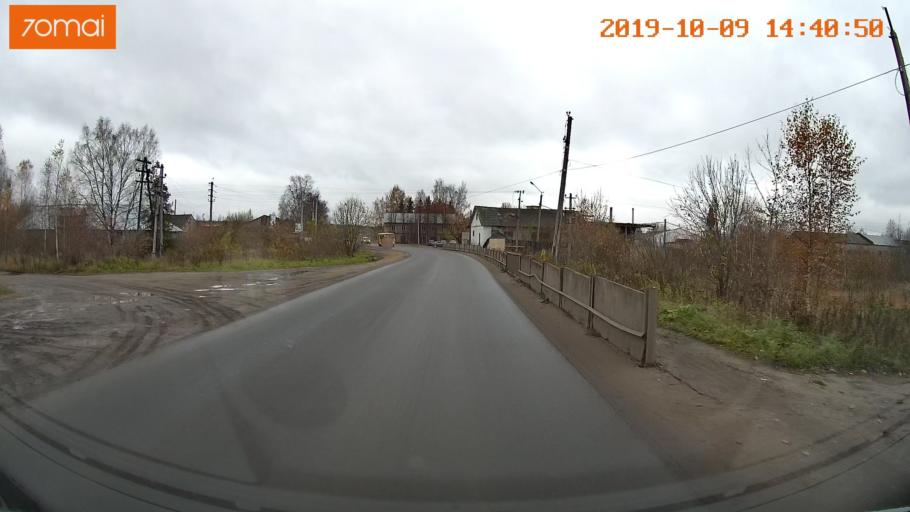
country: RU
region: Kostroma
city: Buy
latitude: 58.4747
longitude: 41.5284
